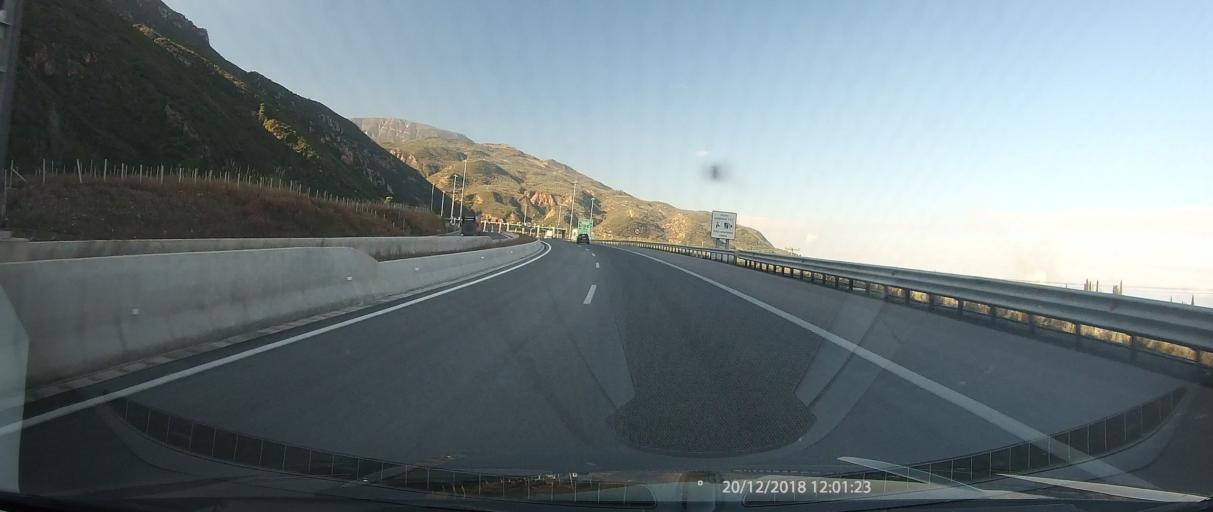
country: GR
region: West Greece
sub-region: Nomos Achaias
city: Temeni
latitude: 38.1899
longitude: 22.1710
